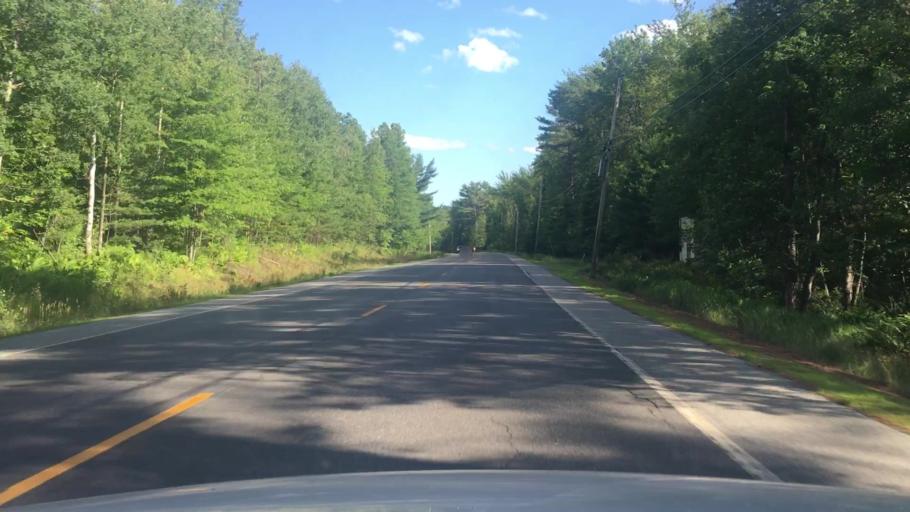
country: US
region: Maine
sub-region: Franklin County
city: Jay
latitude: 44.5298
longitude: -70.2316
